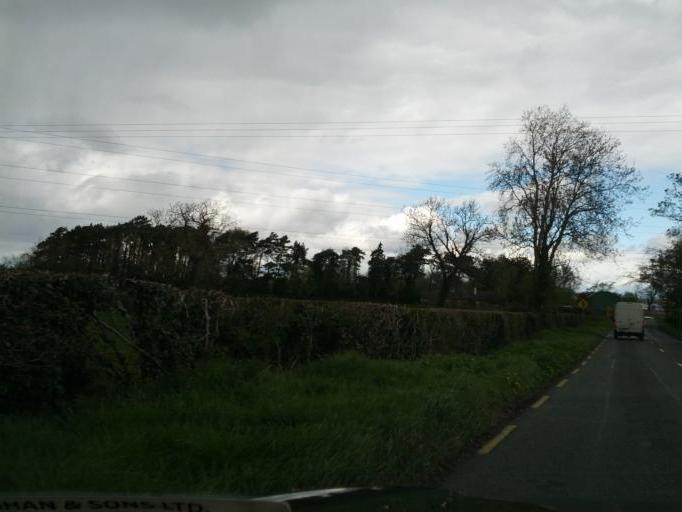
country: IE
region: Leinster
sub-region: An Mhi
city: Dunboyne
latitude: 53.3873
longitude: -6.4514
